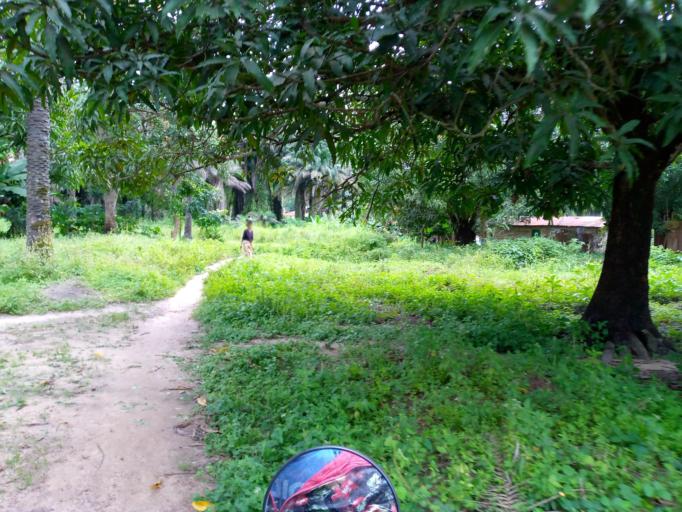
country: SL
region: Northern Province
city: Binkolo
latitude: 9.1098
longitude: -12.2051
